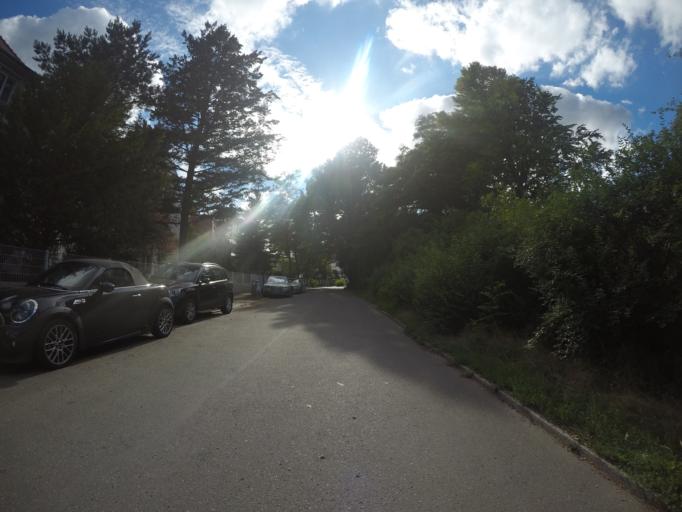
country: DE
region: Berlin
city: Dahlem
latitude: 52.4551
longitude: 13.2776
